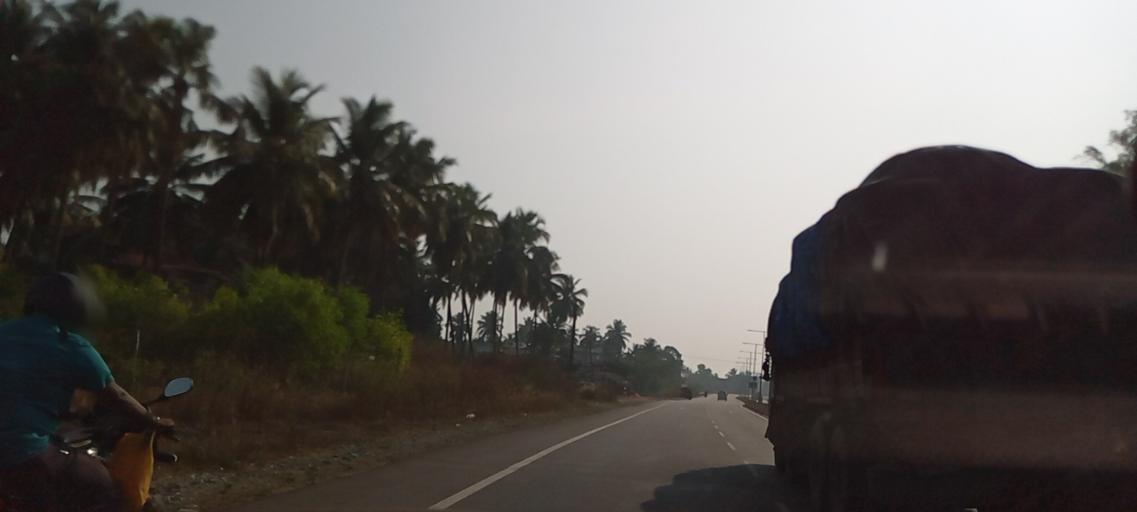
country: IN
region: Karnataka
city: Gangolli
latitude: 13.6783
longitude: 74.6934
